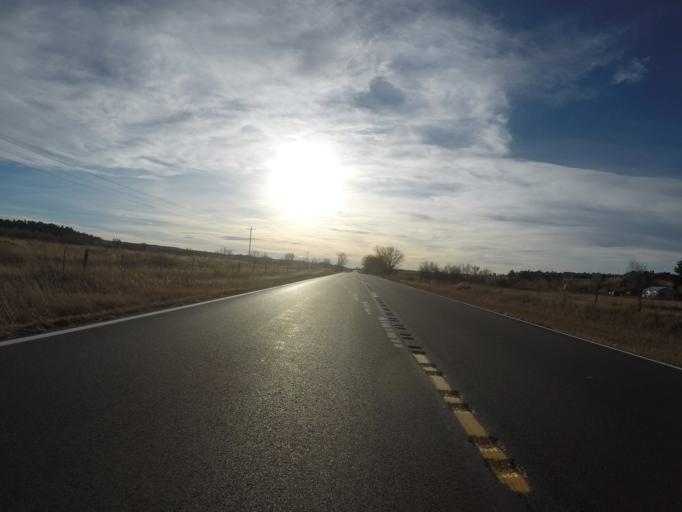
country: US
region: Montana
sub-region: Musselshell County
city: Roundup
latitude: 46.3777
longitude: -108.6339
